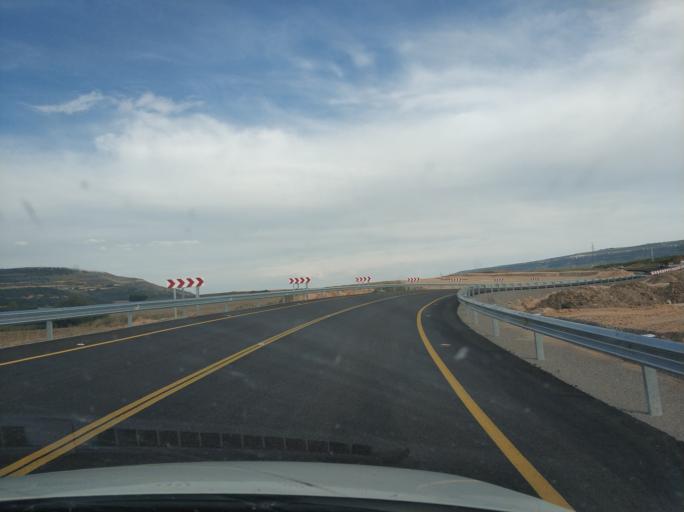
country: ES
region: Castille and Leon
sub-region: Provincia de Palencia
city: Pomar de Valdivia
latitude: 42.7584
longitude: -4.1806
